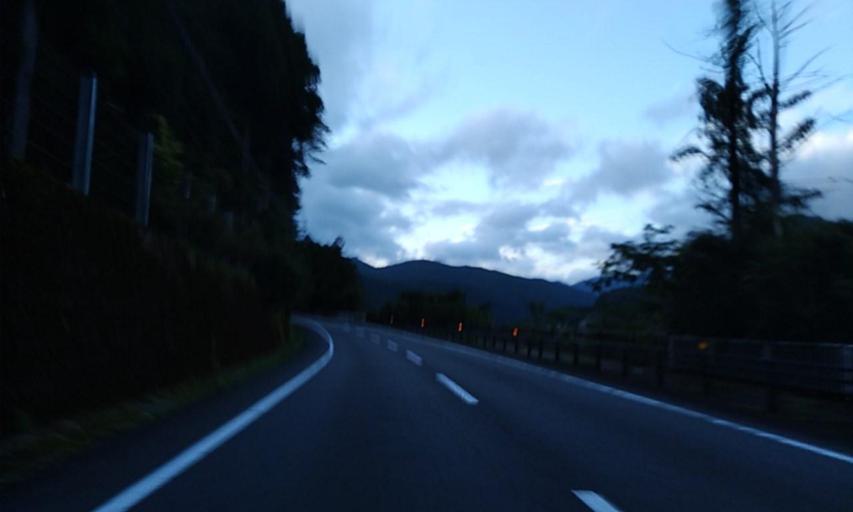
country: JP
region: Wakayama
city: Shingu
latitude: 33.7301
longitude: 135.9482
